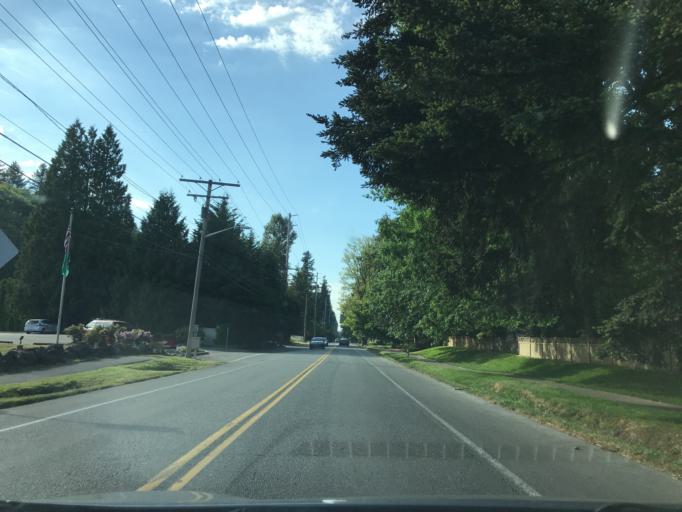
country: US
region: Washington
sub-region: King County
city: Issaquah
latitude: 47.5320
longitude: -122.0428
